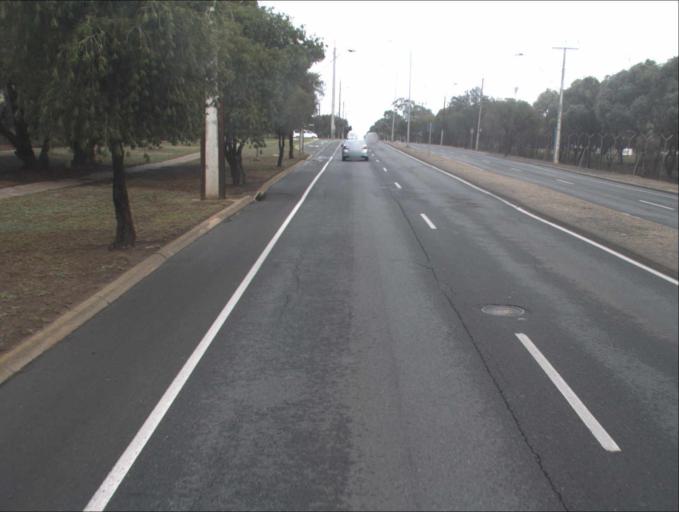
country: AU
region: South Australia
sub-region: Salisbury
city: Ingle Farm
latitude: -34.8471
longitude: 138.6311
